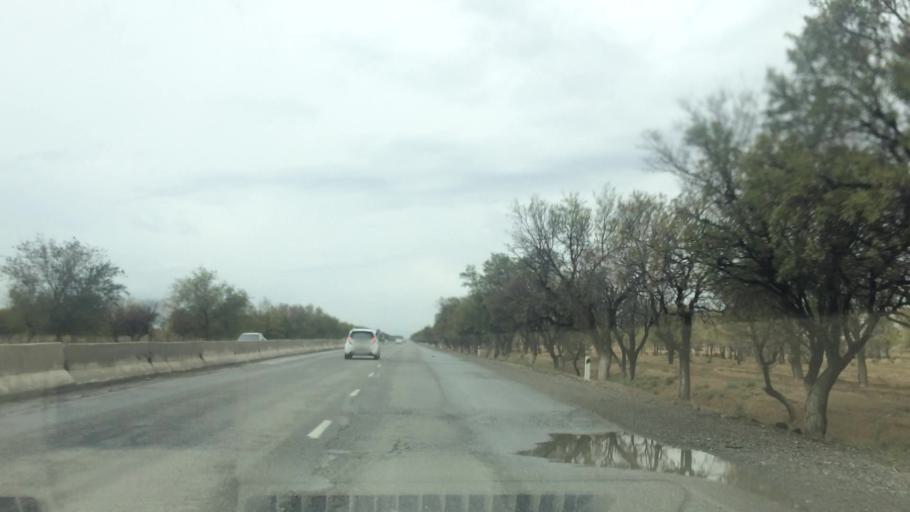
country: UZ
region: Samarqand
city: Bulung'ur
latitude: 39.8317
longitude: 67.4148
